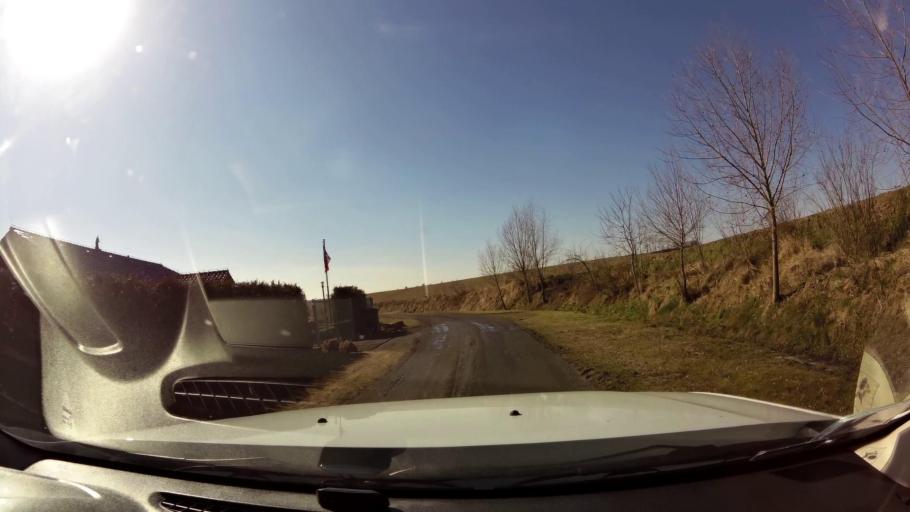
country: PL
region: West Pomeranian Voivodeship
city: Trzcinsko Zdroj
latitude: 52.9948
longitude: 14.6028
